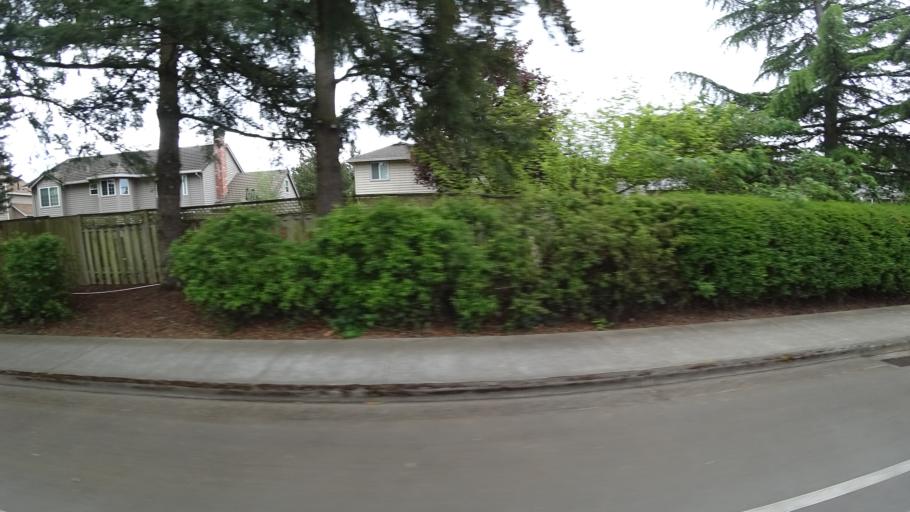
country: US
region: Oregon
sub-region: Washington County
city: Hillsboro
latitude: 45.5379
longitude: -122.9843
